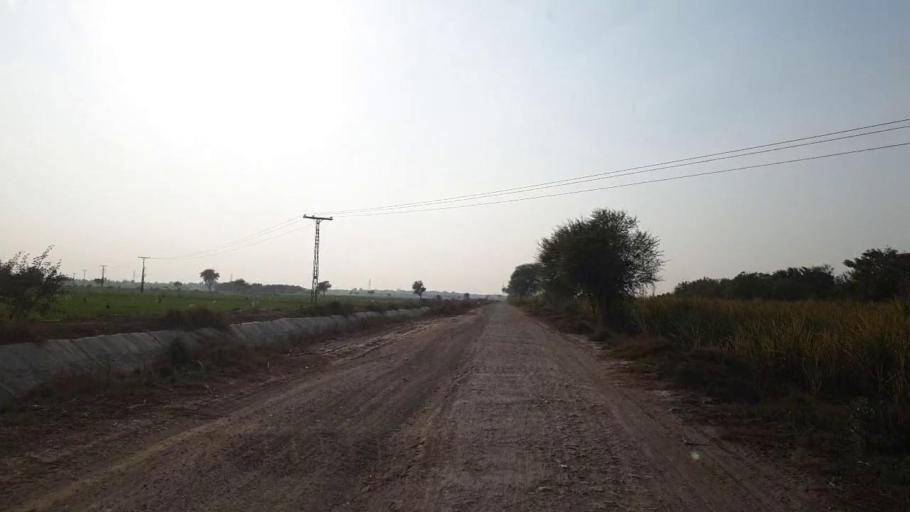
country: PK
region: Sindh
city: Matiari
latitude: 25.5915
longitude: 68.4722
